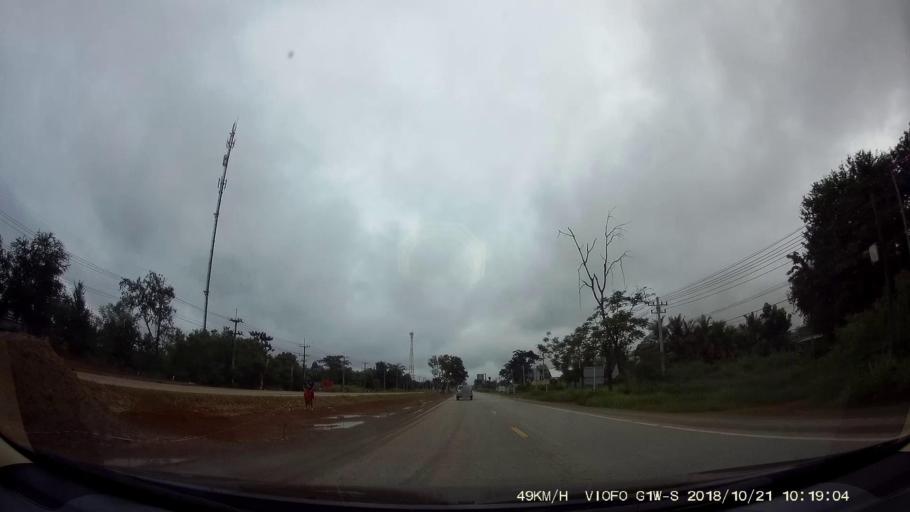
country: TH
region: Chaiyaphum
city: Phu Khiao
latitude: 16.3177
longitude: 102.1961
